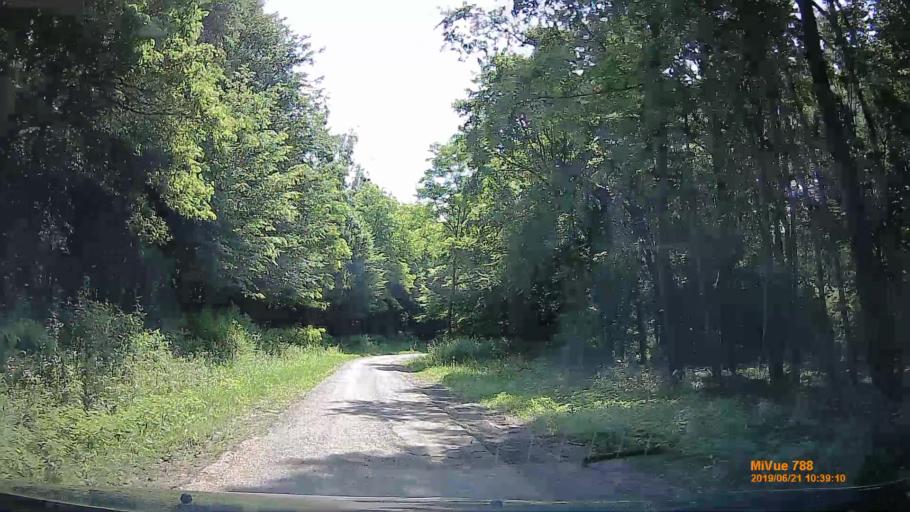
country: HU
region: Baranya
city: Buekkoesd
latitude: 46.1349
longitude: 17.9862
